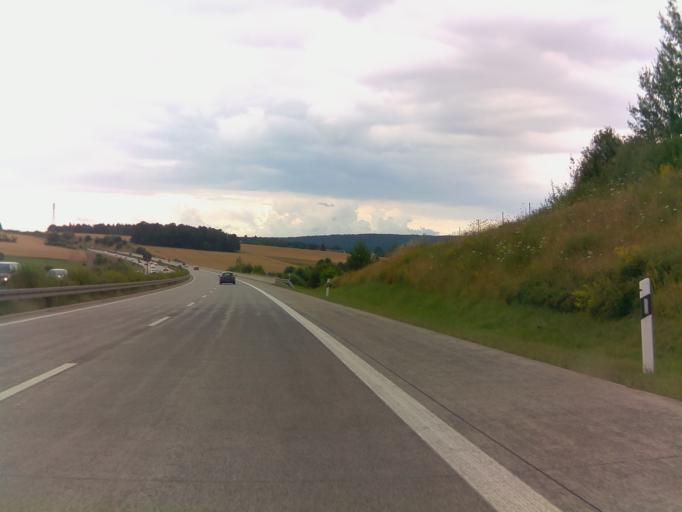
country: DE
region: Thuringia
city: Ritschenhausen
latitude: 50.5007
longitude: 10.4424
